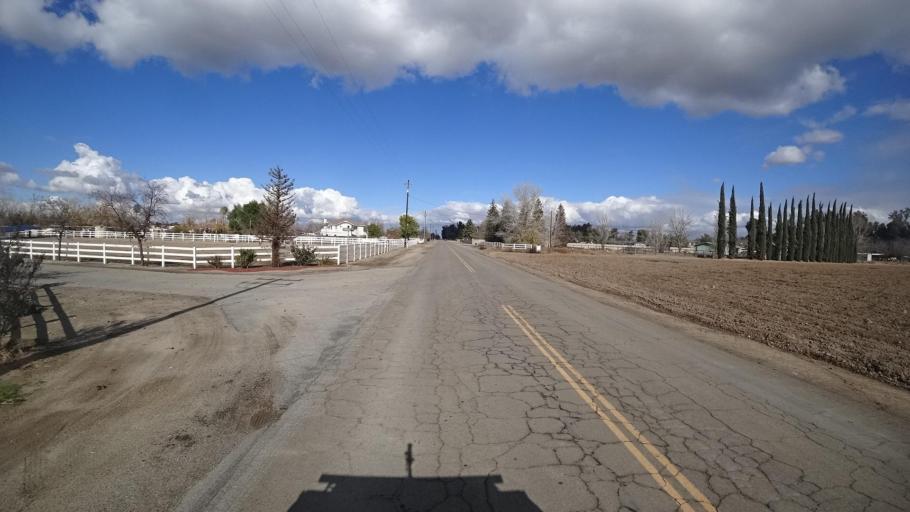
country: US
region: California
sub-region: Kern County
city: Greenfield
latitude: 35.2247
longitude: -119.0923
